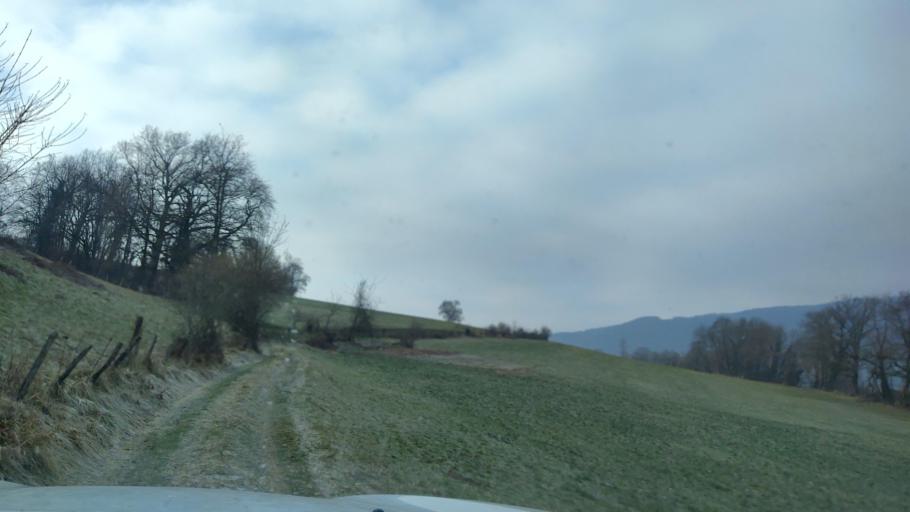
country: FR
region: Rhone-Alpes
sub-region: Departement de la Savoie
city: La Biolle
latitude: 45.7466
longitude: 5.9459
